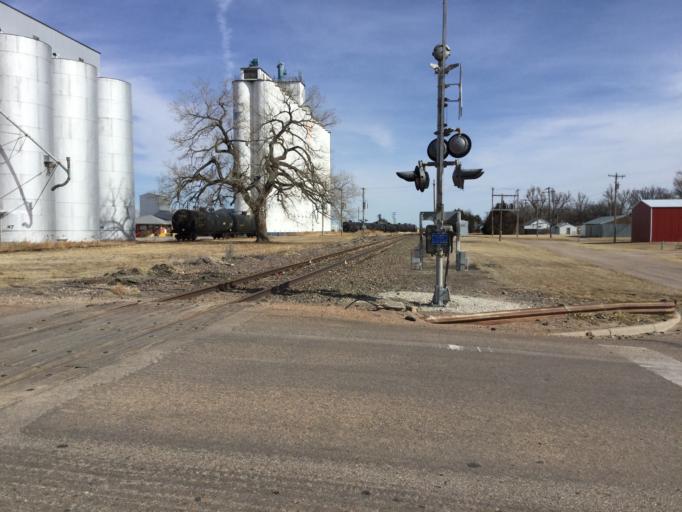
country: US
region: Kansas
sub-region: Barton County
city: Ellinwood
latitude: 38.5145
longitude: -98.3973
